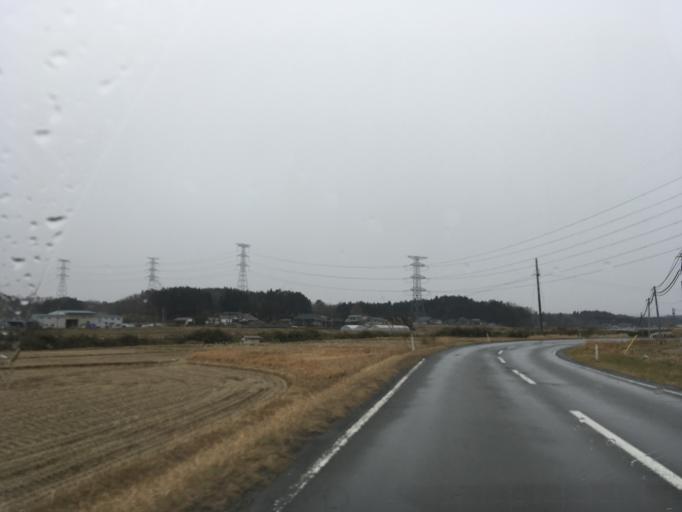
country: JP
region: Iwate
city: Ichinoseki
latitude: 38.8530
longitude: 141.0871
